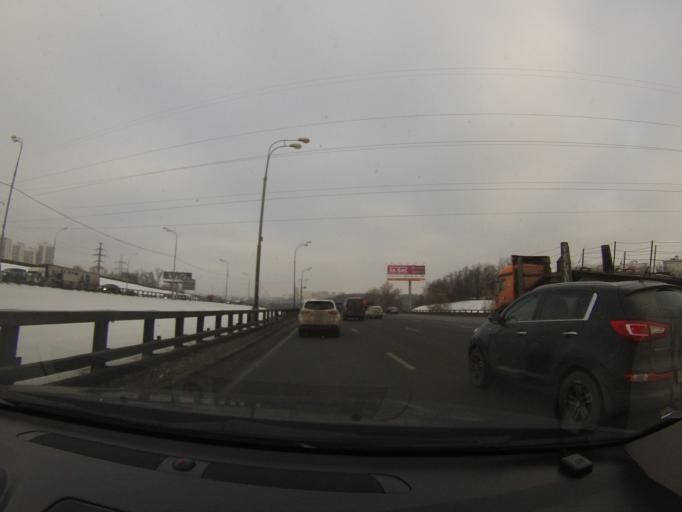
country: RU
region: Moscow
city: Strogino
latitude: 55.8370
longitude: 37.3967
